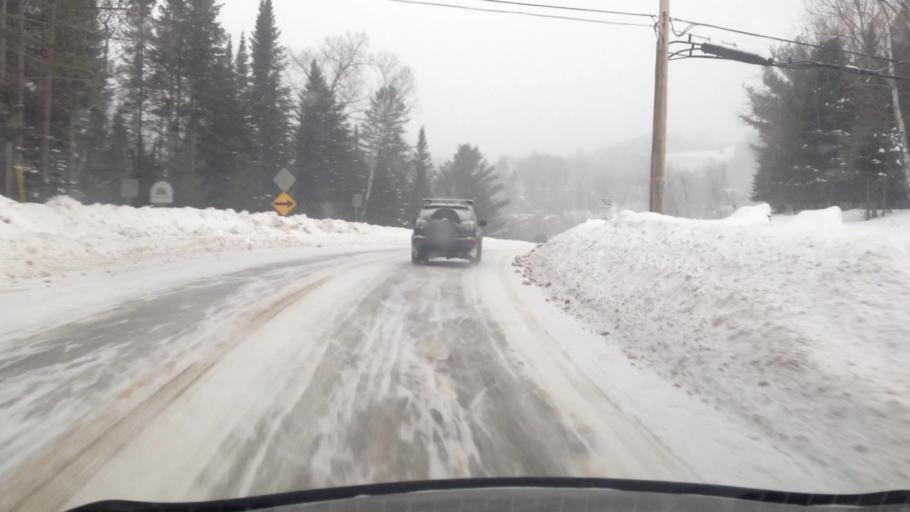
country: CA
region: Quebec
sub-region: Laurentides
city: Mont-Tremblant
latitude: 45.9730
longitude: -74.6309
